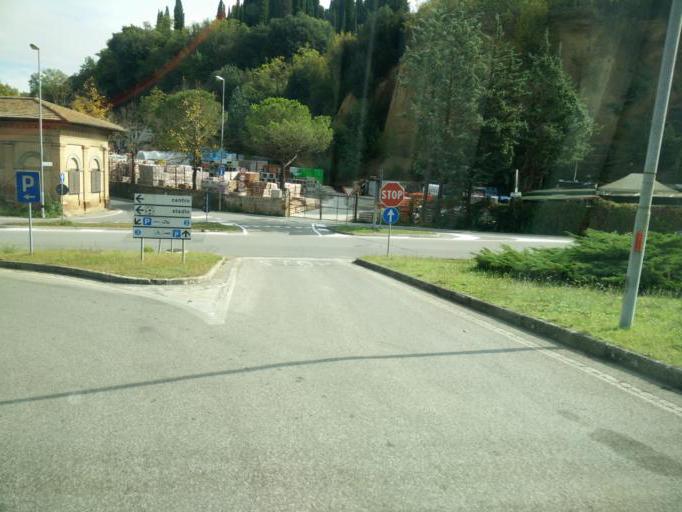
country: IT
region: Tuscany
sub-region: Provincia di Siena
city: Siena
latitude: 43.3141
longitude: 11.3174
